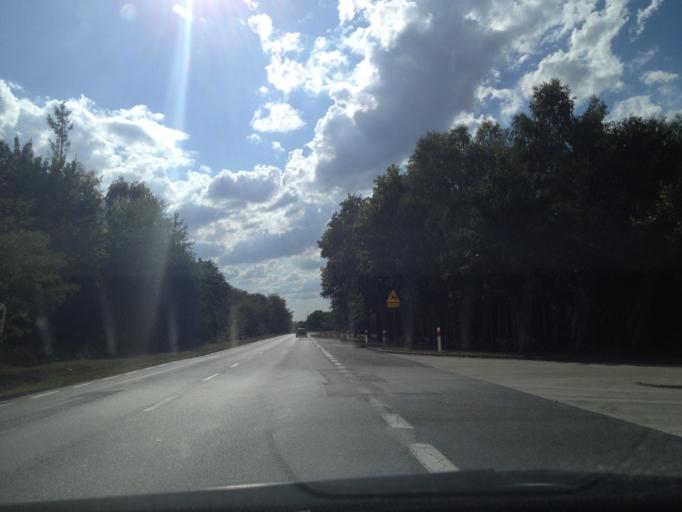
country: PL
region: Lubusz
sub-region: Powiat zarski
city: Sieniawa Zarska
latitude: 51.6312
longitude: 15.0960
